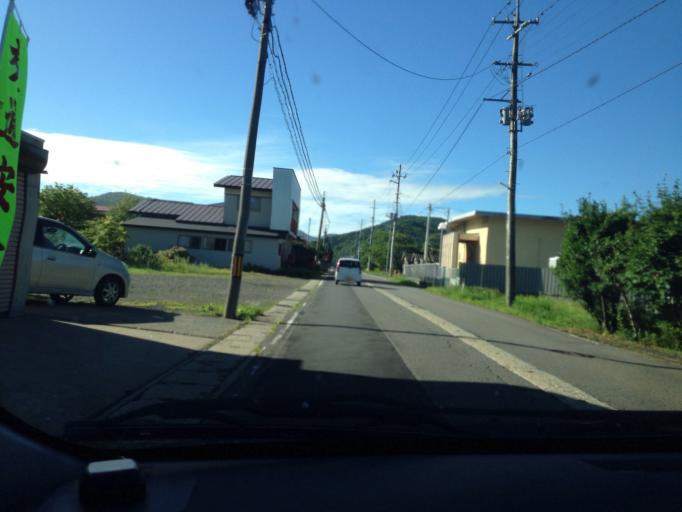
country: JP
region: Fukushima
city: Inawashiro
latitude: 37.4010
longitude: 140.1296
